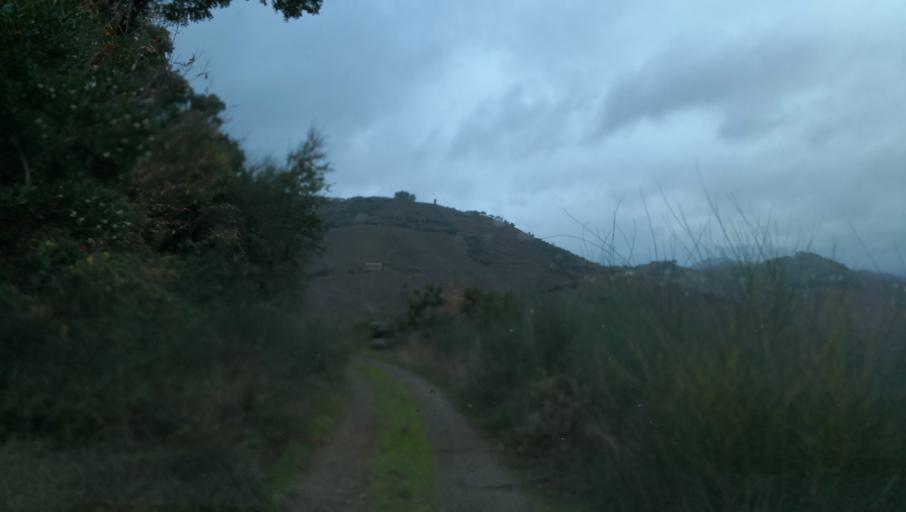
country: PT
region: Vila Real
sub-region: Santa Marta de Penaguiao
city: Santa Marta de Penaguiao
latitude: 41.2270
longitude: -7.7453
